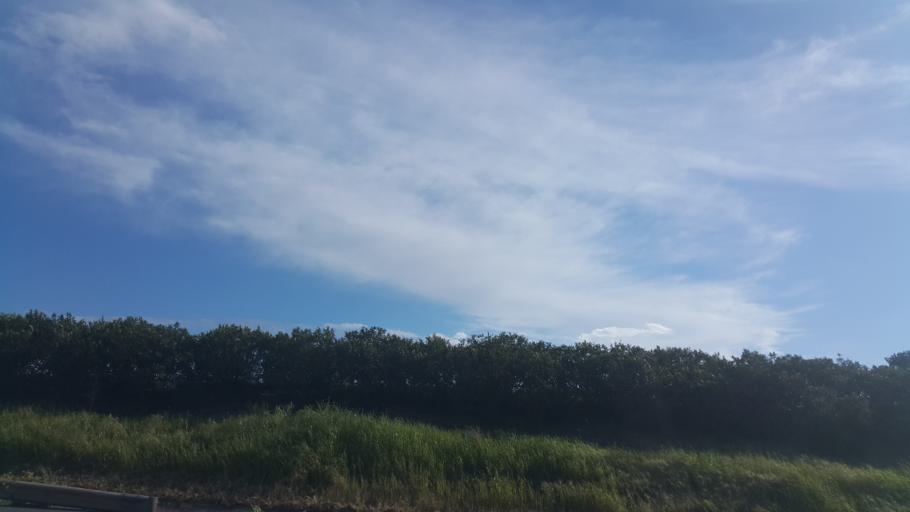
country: TR
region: Adana
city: Yakapinar
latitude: 36.9954
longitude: 35.5740
